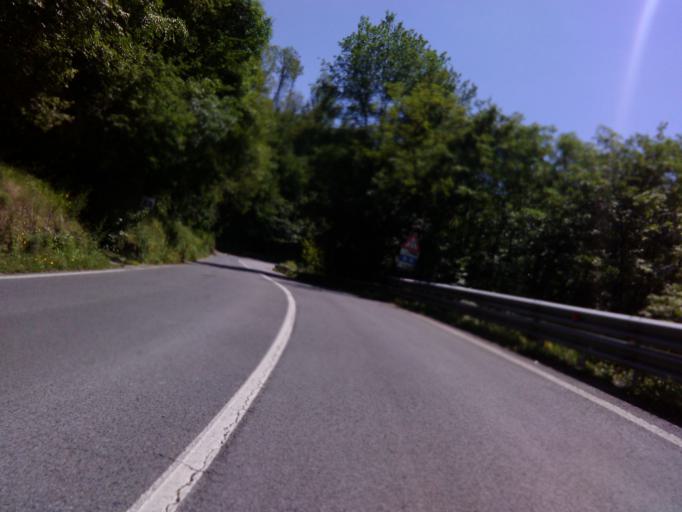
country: IT
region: Tuscany
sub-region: Provincia di Massa-Carrara
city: Barbarasco
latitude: 44.2695
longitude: 9.9529
